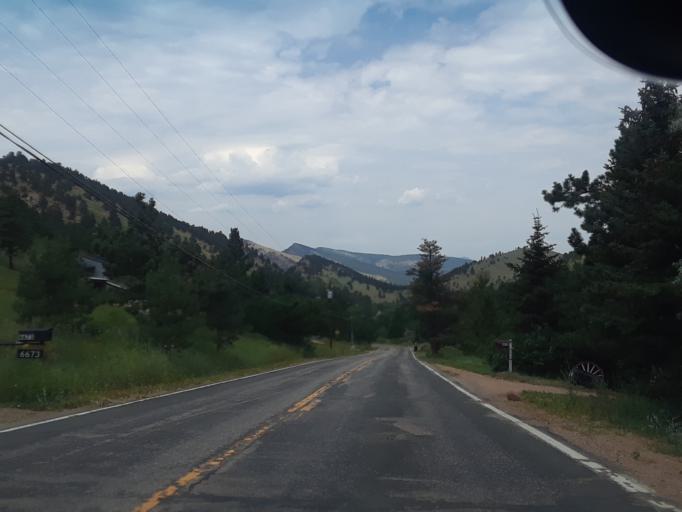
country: US
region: Colorado
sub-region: Boulder County
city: Boulder
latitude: 40.0953
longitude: -105.3020
